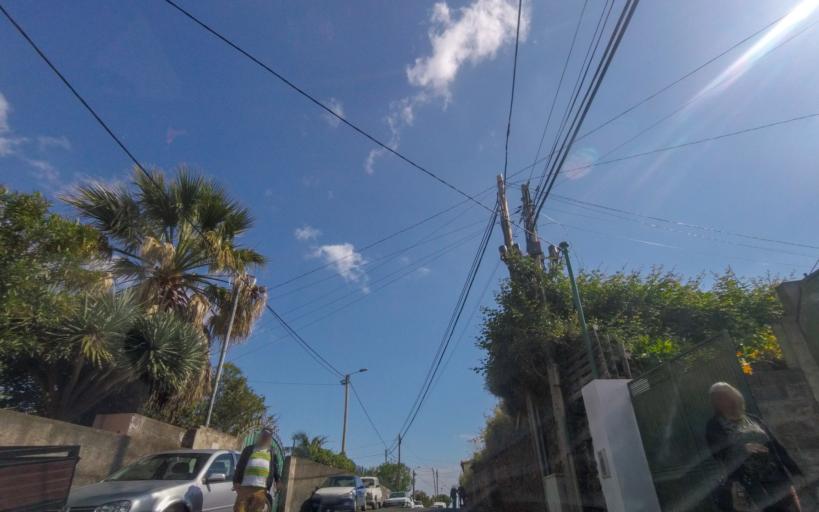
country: PT
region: Madeira
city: Camara de Lobos
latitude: 32.6732
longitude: -16.9470
